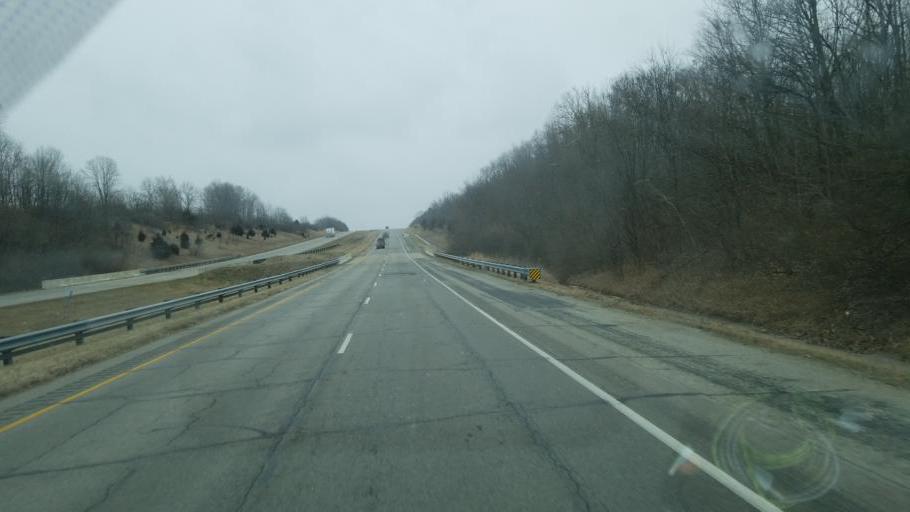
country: US
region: Indiana
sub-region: Wabash County
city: Wabash
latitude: 40.8022
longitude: -85.8933
